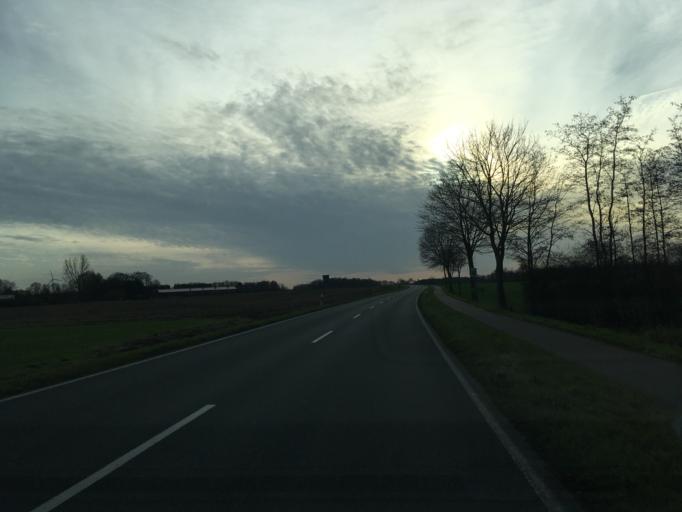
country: DE
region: North Rhine-Westphalia
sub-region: Regierungsbezirk Munster
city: Gescher
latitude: 51.9948
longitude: 7.0361
